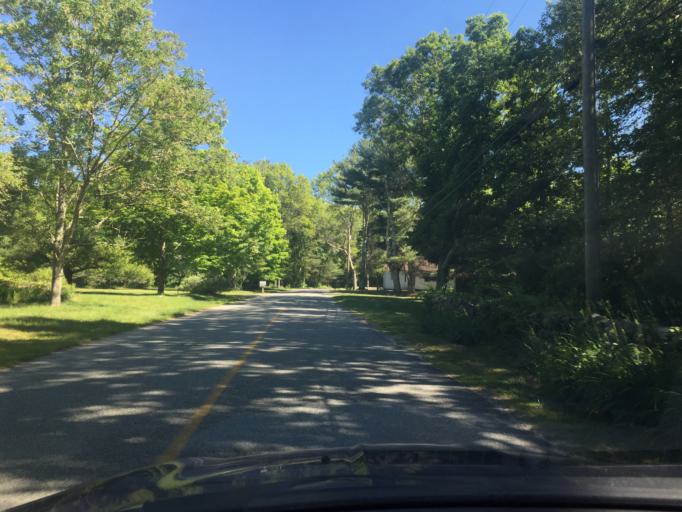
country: US
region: Rhode Island
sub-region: Washington County
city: Hopkinton
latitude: 41.4923
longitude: -71.8098
